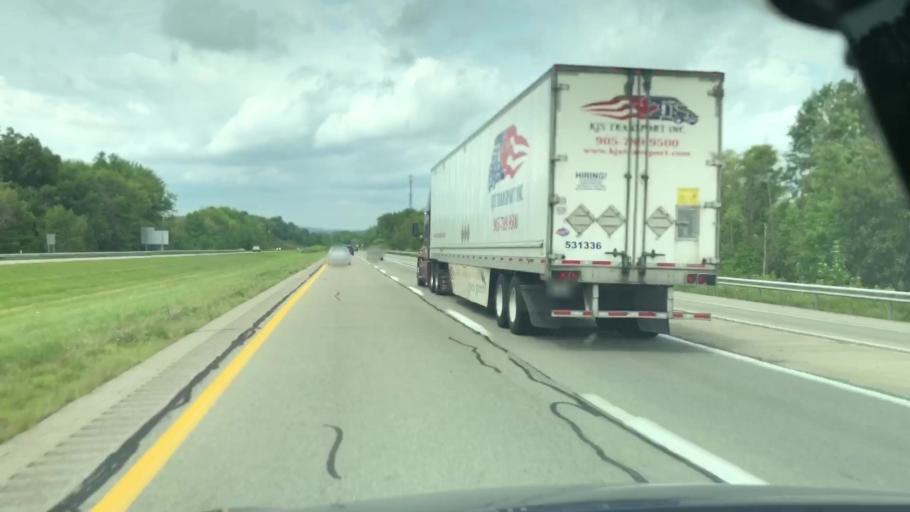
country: US
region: Pennsylvania
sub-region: Crawford County
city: Meadville
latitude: 41.7180
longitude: -80.2014
